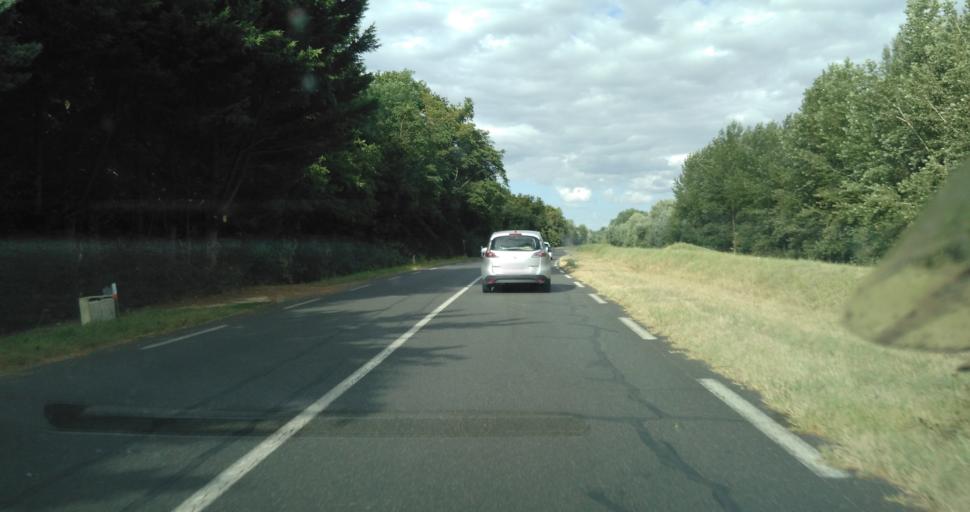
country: FR
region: Centre
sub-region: Departement d'Indre-et-Loire
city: Huismes
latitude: 47.2765
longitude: 0.3099
